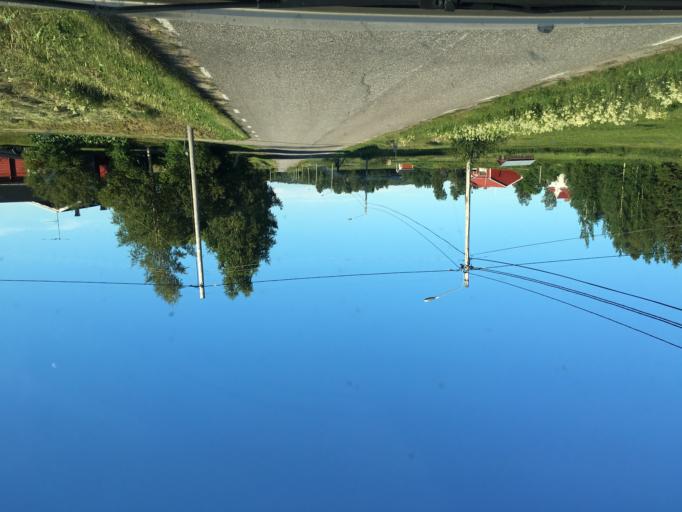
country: SE
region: Norrbotten
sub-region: Kalix Kommun
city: Rolfs
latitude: 65.8981
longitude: 22.9376
